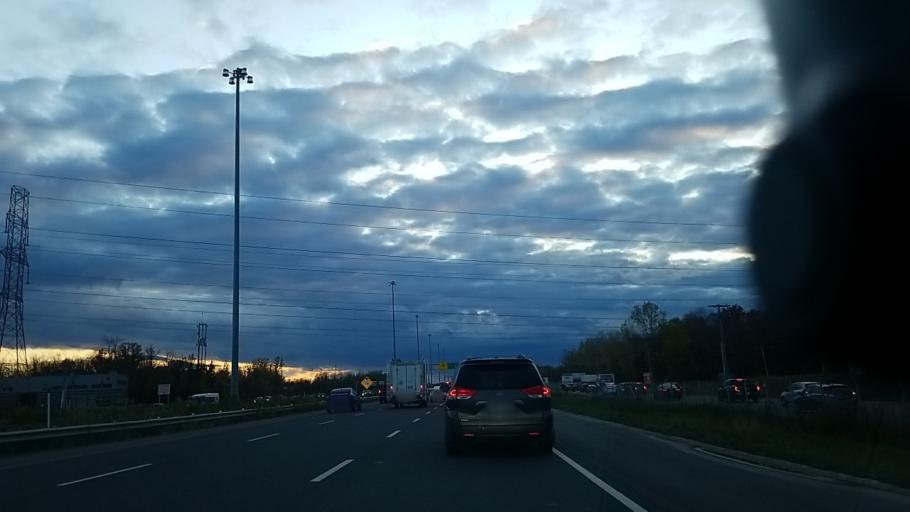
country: CA
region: Quebec
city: Dollard-Des Ormeaux
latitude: 45.5572
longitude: -73.8006
